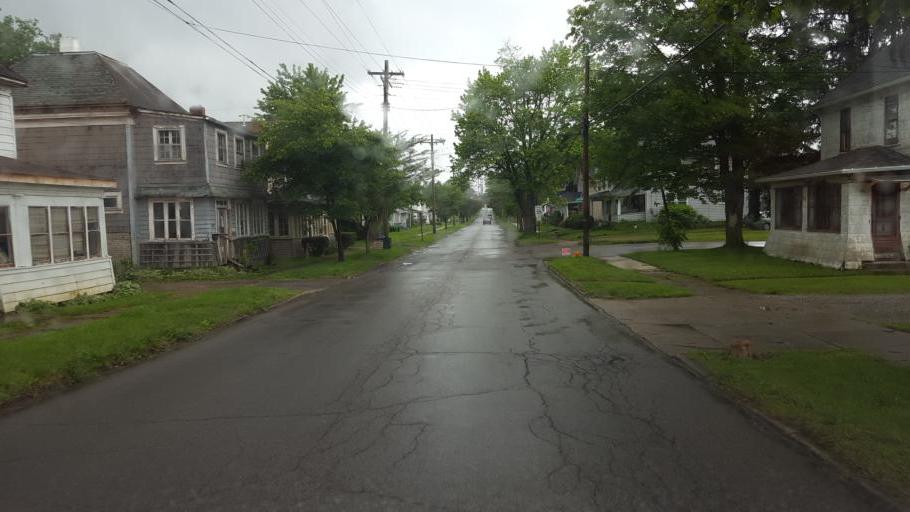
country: US
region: Ohio
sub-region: Ashland County
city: Ashland
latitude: 40.8750
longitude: -82.3071
